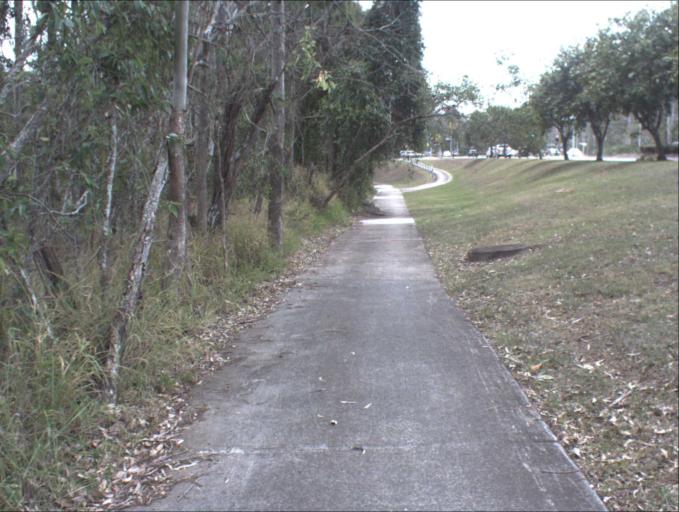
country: AU
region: Queensland
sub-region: Logan
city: Slacks Creek
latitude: -27.6584
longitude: 153.1418
